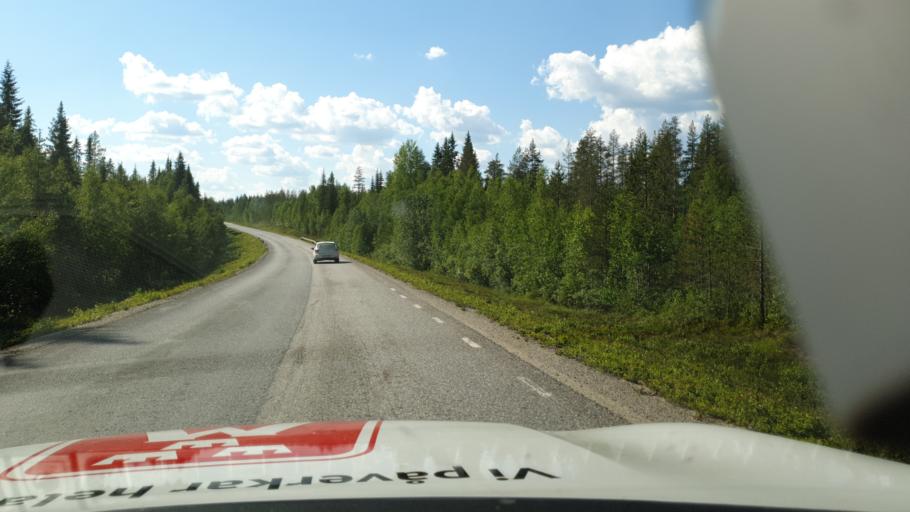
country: SE
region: Vaesterbotten
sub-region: Vindelns Kommun
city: Vindeln
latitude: 64.2552
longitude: 19.8925
